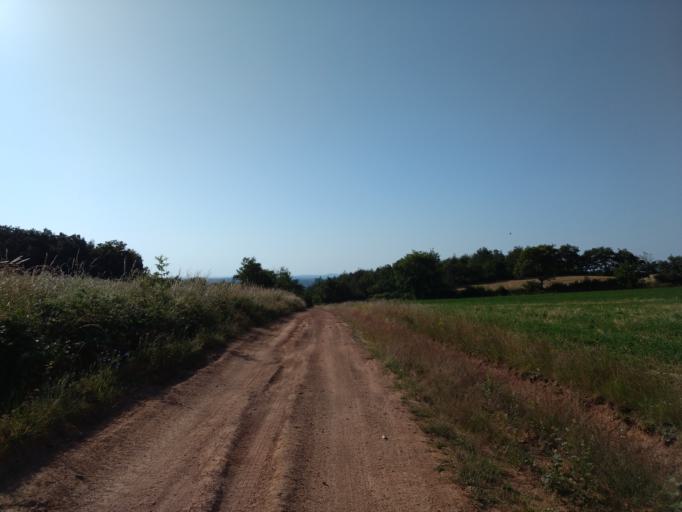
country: FR
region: Midi-Pyrenees
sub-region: Departement de l'Aveyron
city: La Loubiere
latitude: 44.3627
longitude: 2.7031
